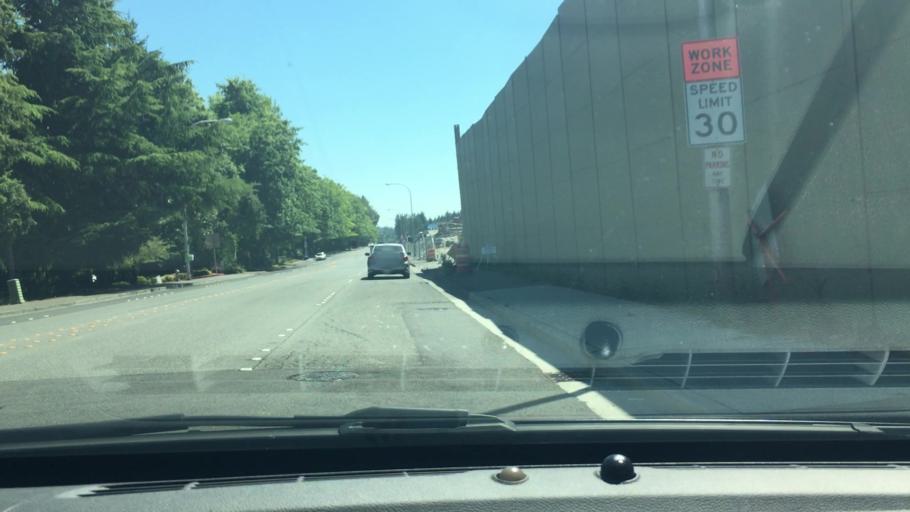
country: US
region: Washington
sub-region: King County
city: Bellevue
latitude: 47.6089
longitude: -122.1909
